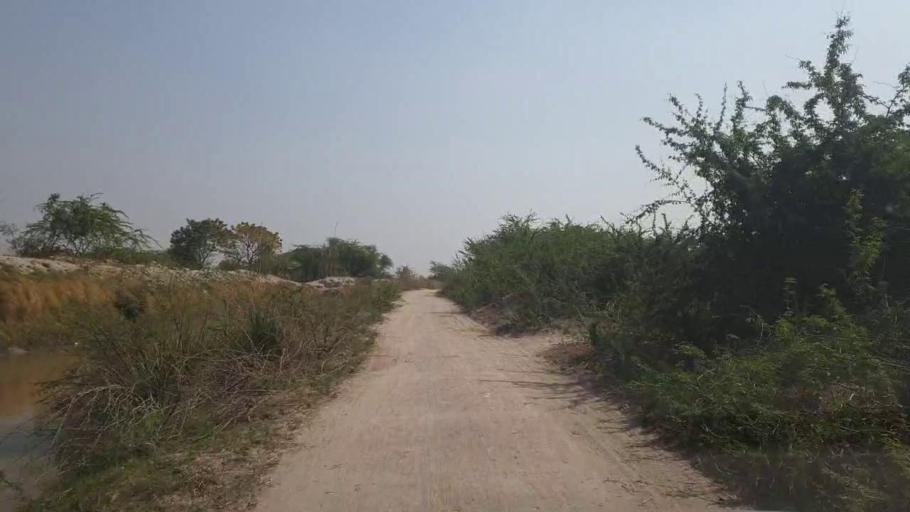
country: PK
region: Sindh
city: Dhoro Naro
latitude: 25.5179
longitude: 69.5383
